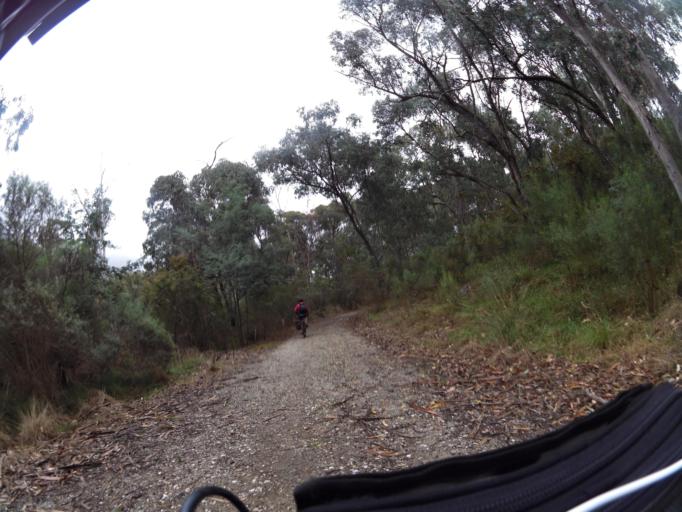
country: AU
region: New South Wales
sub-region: Greater Hume Shire
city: Holbrook
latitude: -36.1688
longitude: 147.4064
